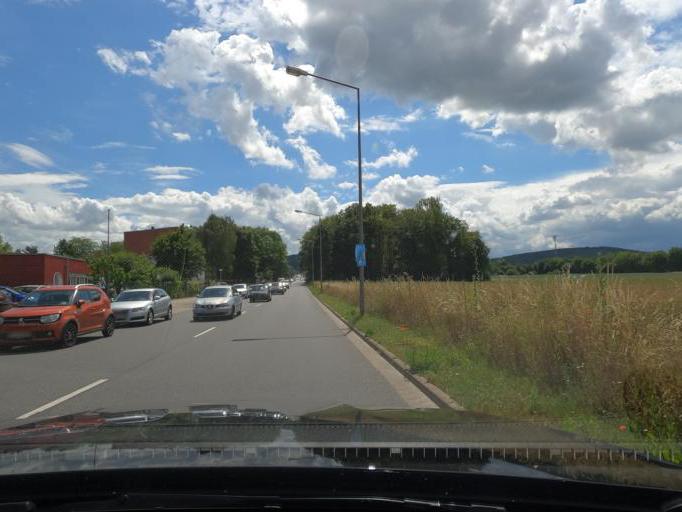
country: DE
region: Lower Saxony
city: Elbe
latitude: 52.1425
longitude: 10.2941
